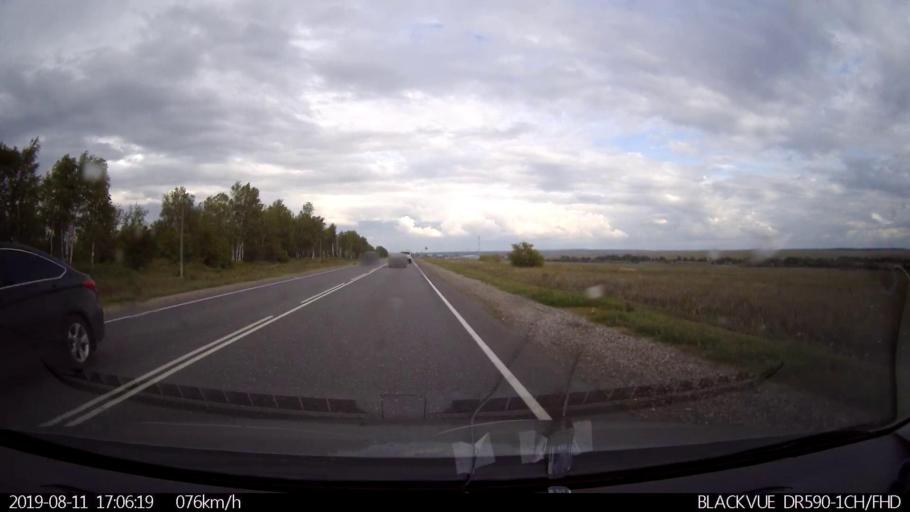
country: RU
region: Ulyanovsk
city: Mayna
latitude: 54.2950
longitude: 47.8038
